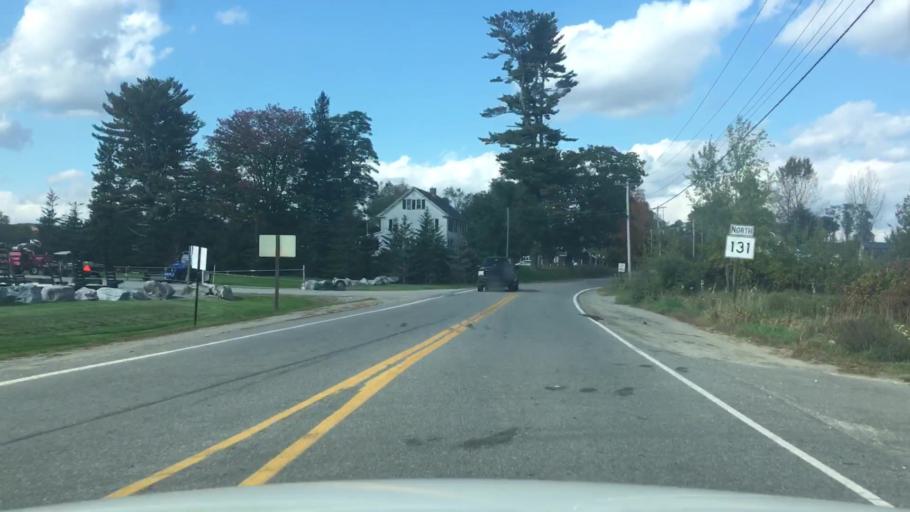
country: US
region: Maine
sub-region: Knox County
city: Union
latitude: 44.2179
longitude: -69.2842
